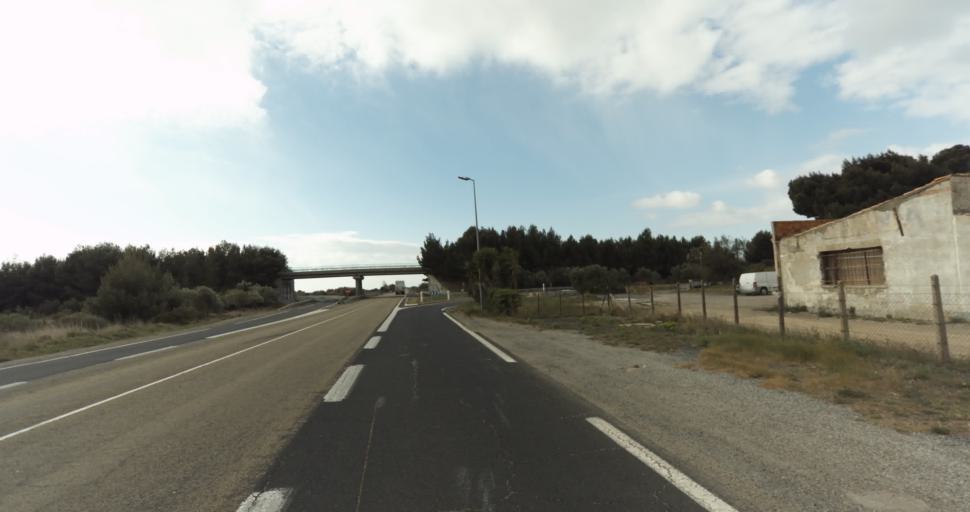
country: FR
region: Languedoc-Roussillon
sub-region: Departement de l'Aude
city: Leucate
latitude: 42.9327
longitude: 2.9922
